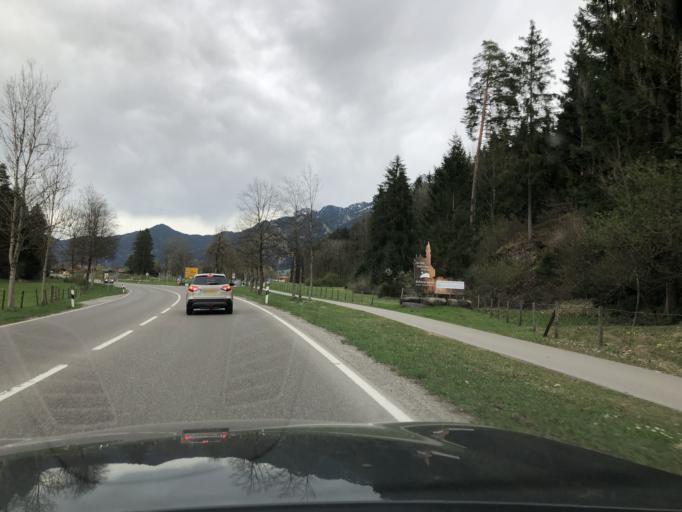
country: DE
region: Bavaria
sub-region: Swabia
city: Fuessen
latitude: 47.5649
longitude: 10.7146
